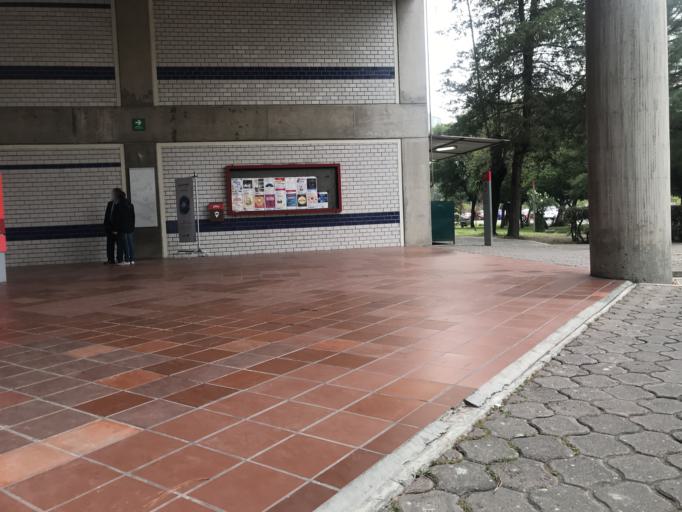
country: MX
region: Puebla
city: Puebla
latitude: 19.0309
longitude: -98.2414
